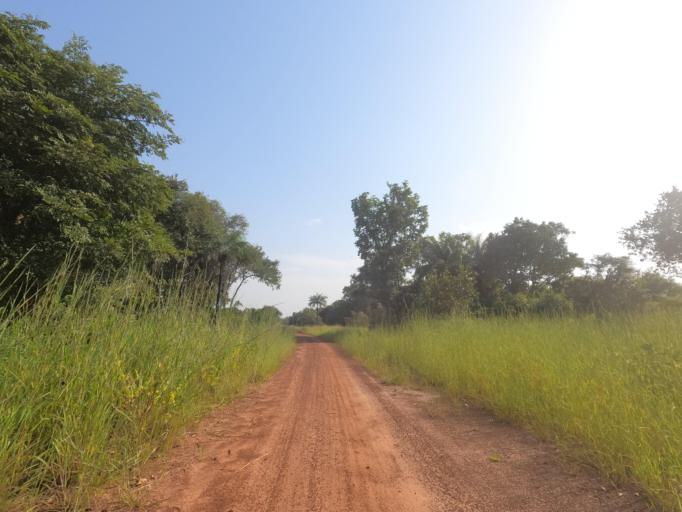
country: SN
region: Sedhiou
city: Sedhiou
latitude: 12.4370
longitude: -15.7382
